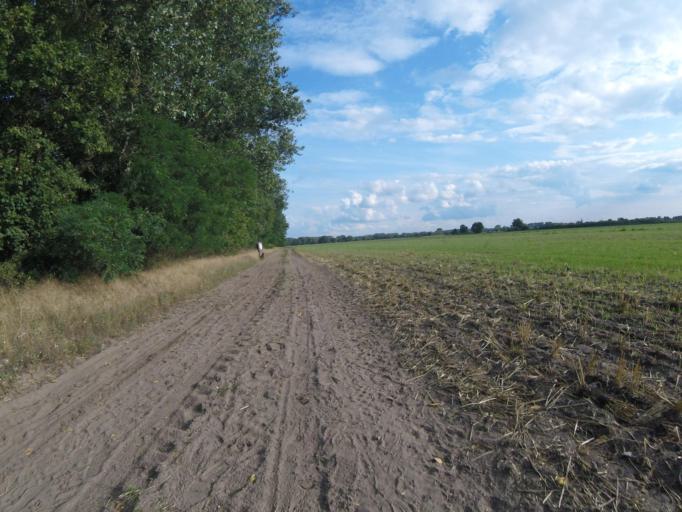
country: DE
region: Brandenburg
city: Mittenwalde
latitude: 52.2852
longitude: 13.5529
